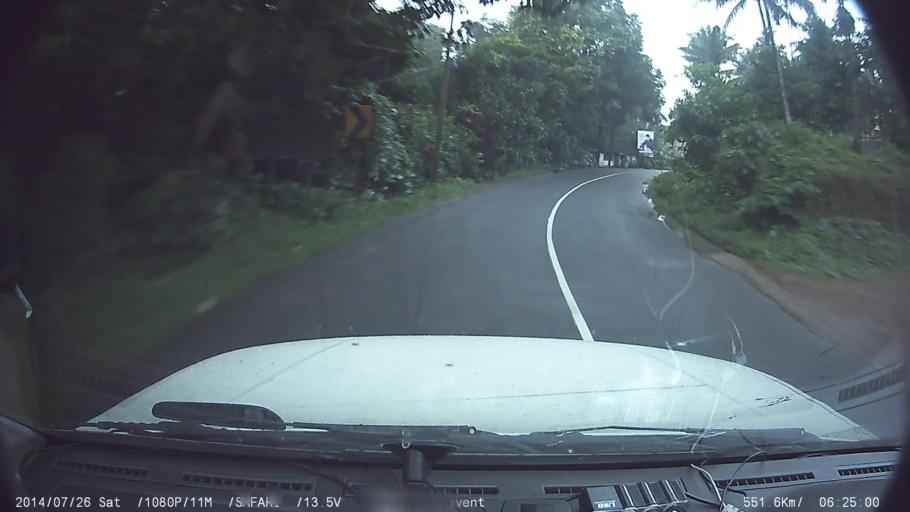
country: IN
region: Kerala
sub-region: Kottayam
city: Palackattumala
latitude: 9.8016
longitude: 76.5748
